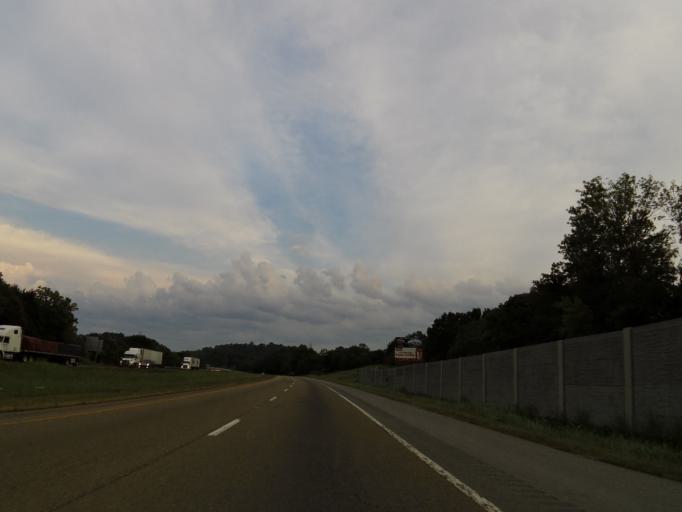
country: US
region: Tennessee
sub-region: Anderson County
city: Rocky Top
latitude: 36.2161
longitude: -84.1445
